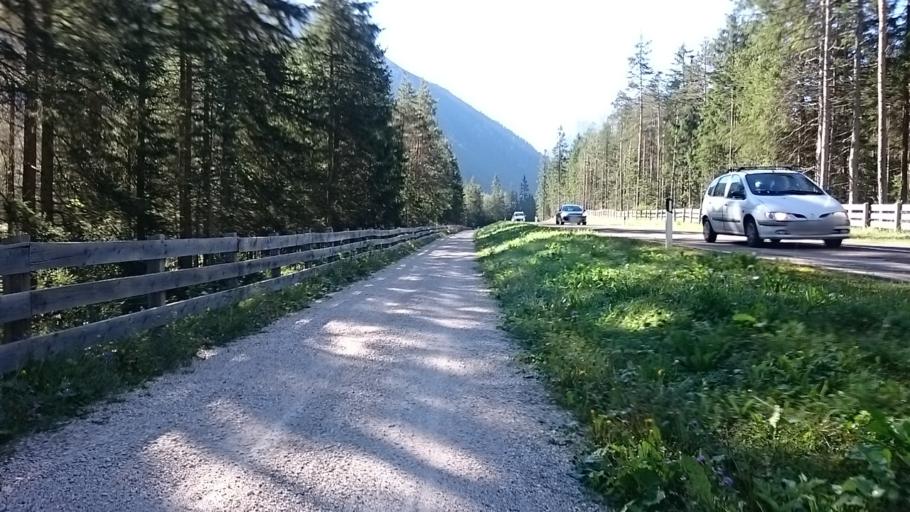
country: IT
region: Trentino-Alto Adige
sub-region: Bolzano
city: Dobbiaco
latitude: 46.6607
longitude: 12.2242
